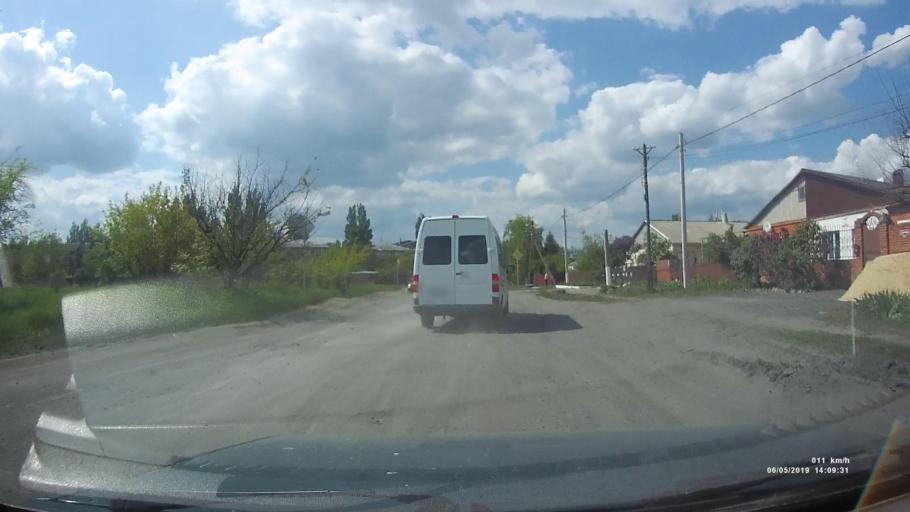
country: RU
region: Rostov
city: Shakhty
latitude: 47.6859
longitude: 40.2917
